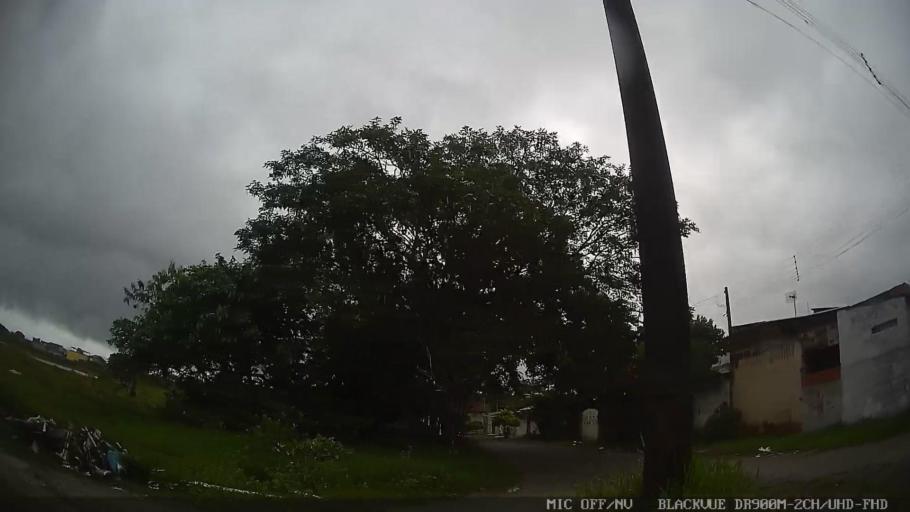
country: BR
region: Sao Paulo
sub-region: Itanhaem
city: Itanhaem
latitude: -24.1838
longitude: -46.8283
